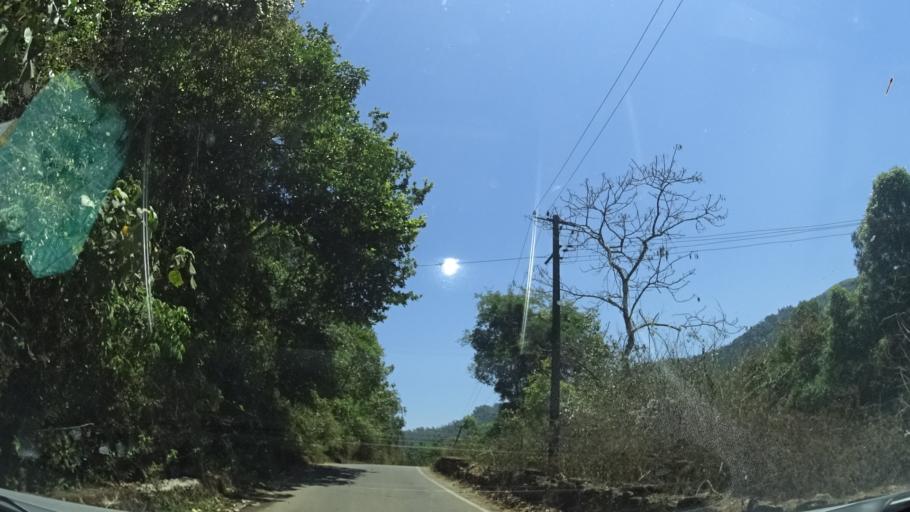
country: IN
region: Karnataka
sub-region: Chikmagalur
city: Sringeri
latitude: 13.1855
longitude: 75.3239
